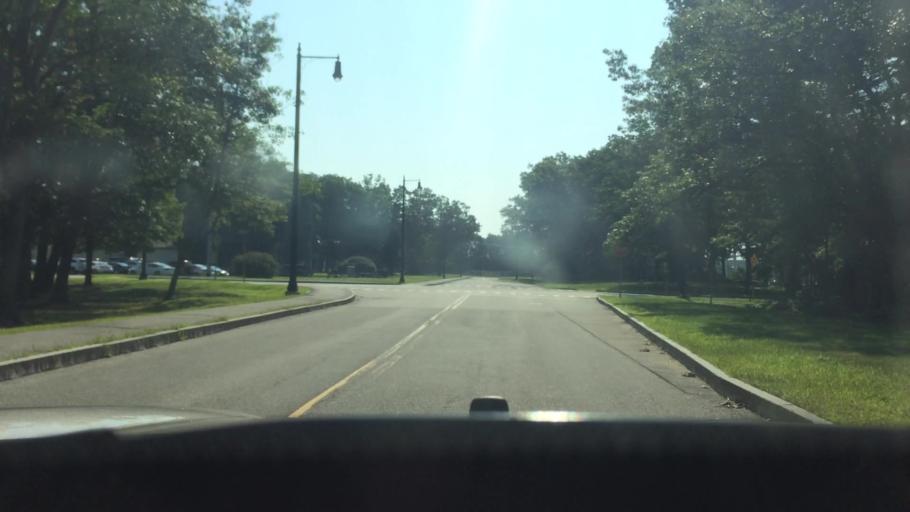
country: US
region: Maine
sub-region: York County
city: South Eliot
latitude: 43.0896
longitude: -70.8176
